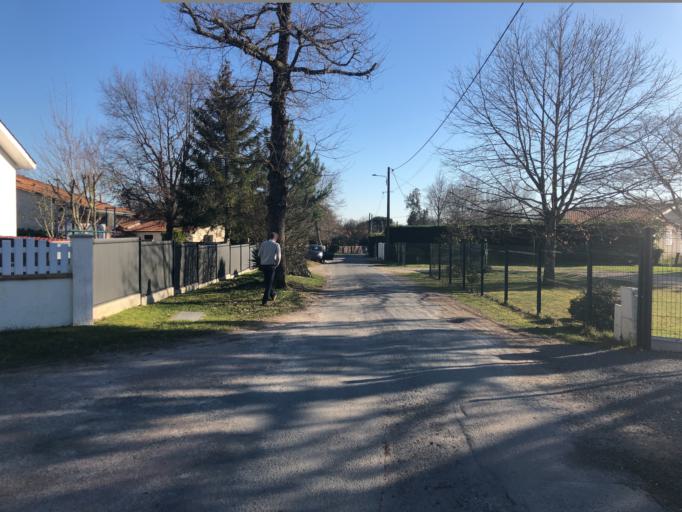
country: FR
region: Aquitaine
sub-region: Departement de la Gironde
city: Castelnau-de-Medoc
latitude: 45.0318
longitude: -0.8037
